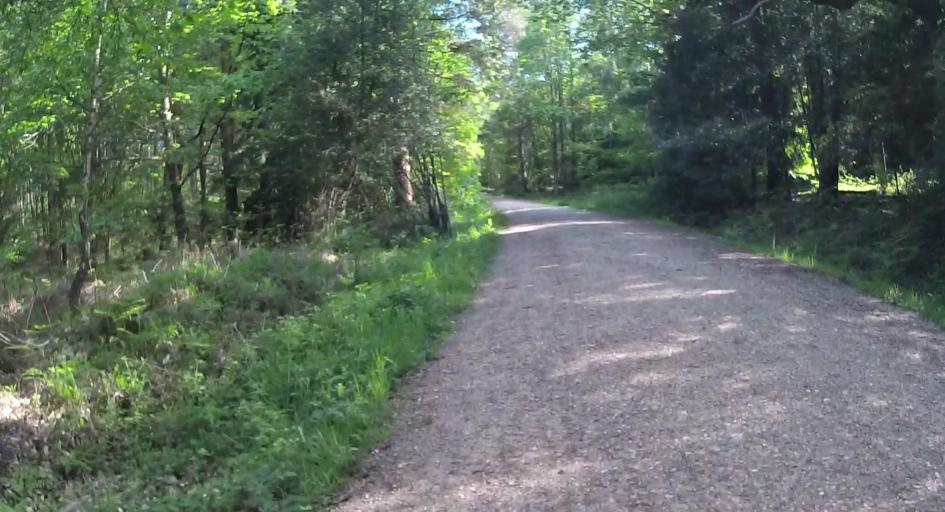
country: GB
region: England
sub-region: Hampshire
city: Lindford
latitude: 51.1629
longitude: -0.8339
